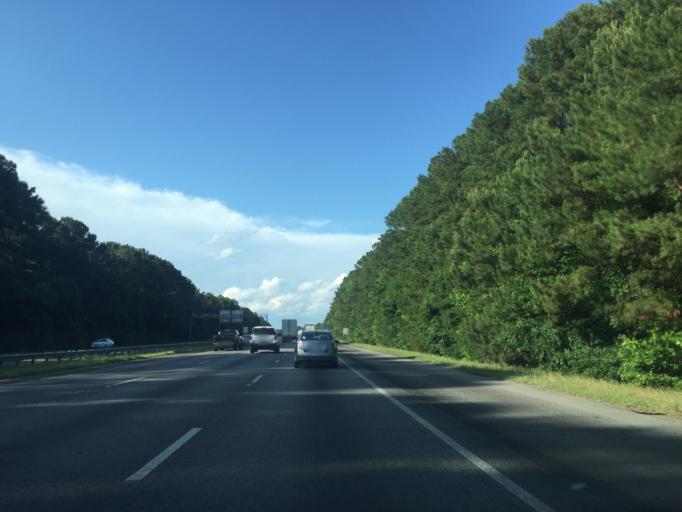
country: US
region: Georgia
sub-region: Chatham County
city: Pooler
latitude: 32.0834
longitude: -81.2413
